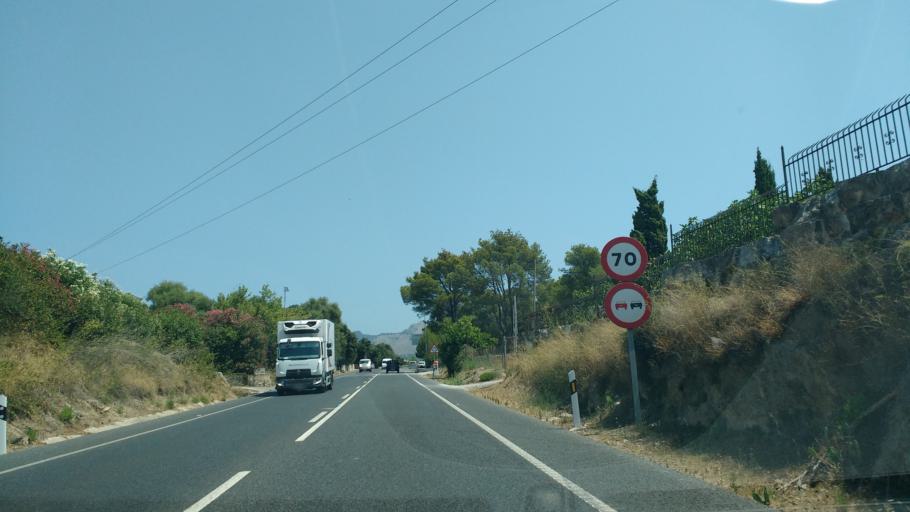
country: ES
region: Balearic Islands
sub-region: Illes Balears
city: Alcudia
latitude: 39.8438
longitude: 3.0890
